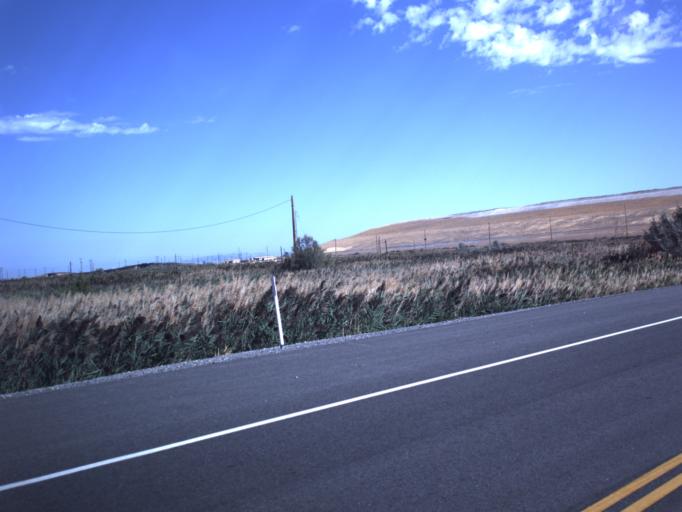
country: US
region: Utah
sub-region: Salt Lake County
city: Magna
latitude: 40.7291
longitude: -112.1705
